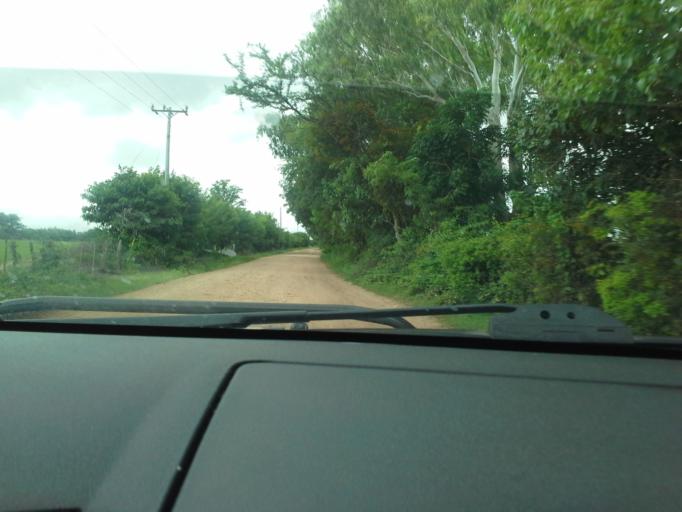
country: NI
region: Matagalpa
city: Ciudad Dario
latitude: 12.8329
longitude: -86.2061
